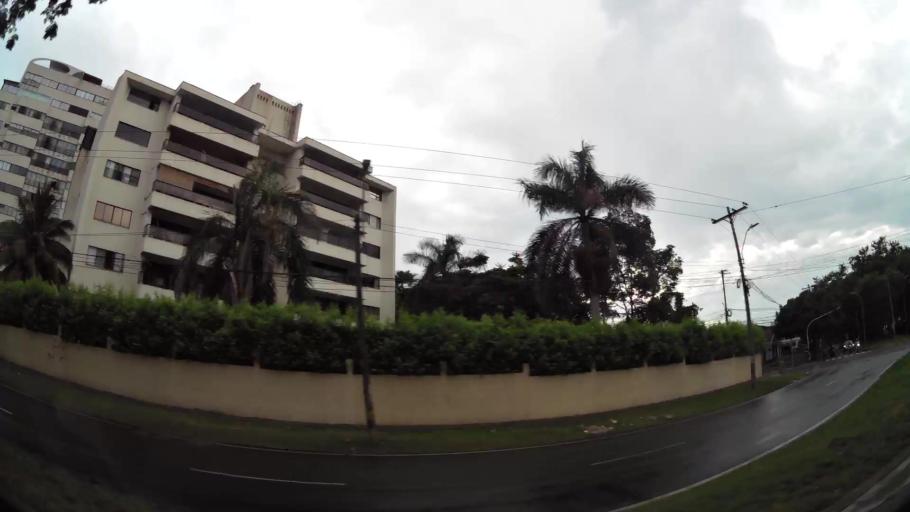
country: CO
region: Valle del Cauca
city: Cali
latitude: 3.4817
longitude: -76.5249
